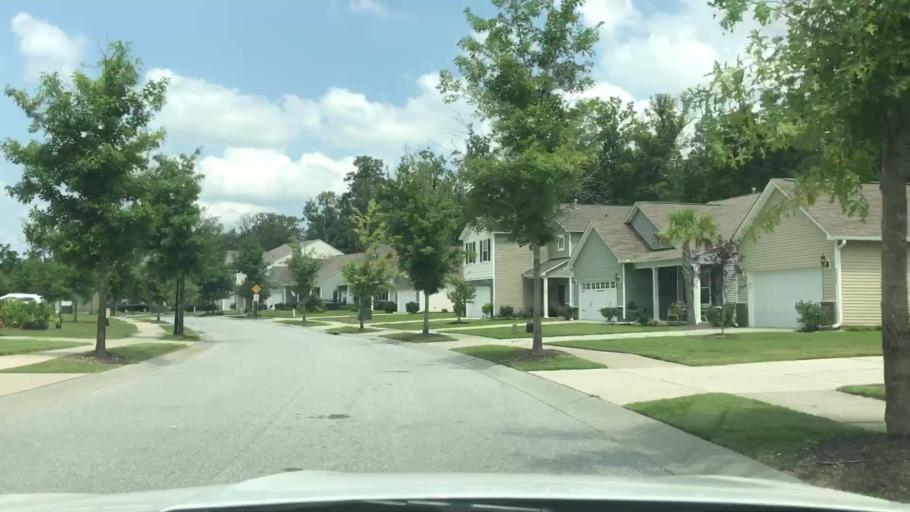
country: US
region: South Carolina
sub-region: Charleston County
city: Shell Point
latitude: 32.8114
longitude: -80.0772
